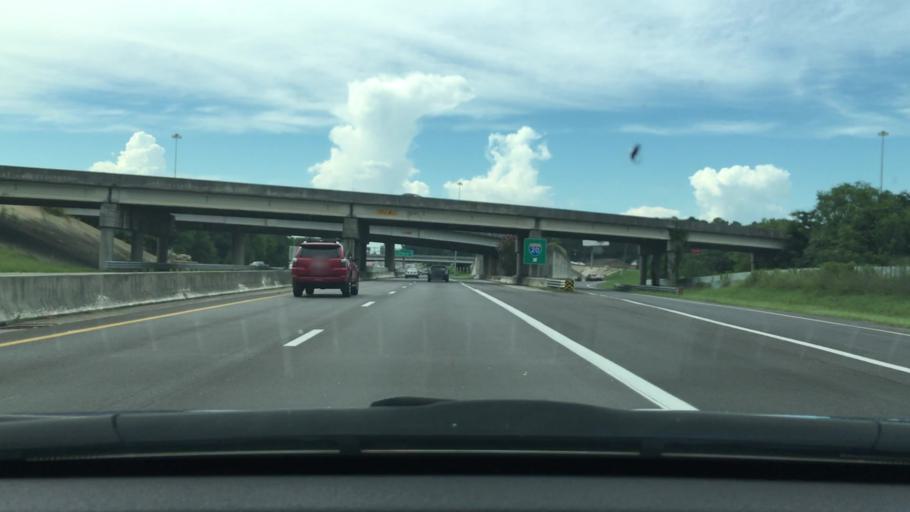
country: US
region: South Carolina
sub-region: Lexington County
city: Saint Andrews
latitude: 34.0272
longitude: -81.1006
